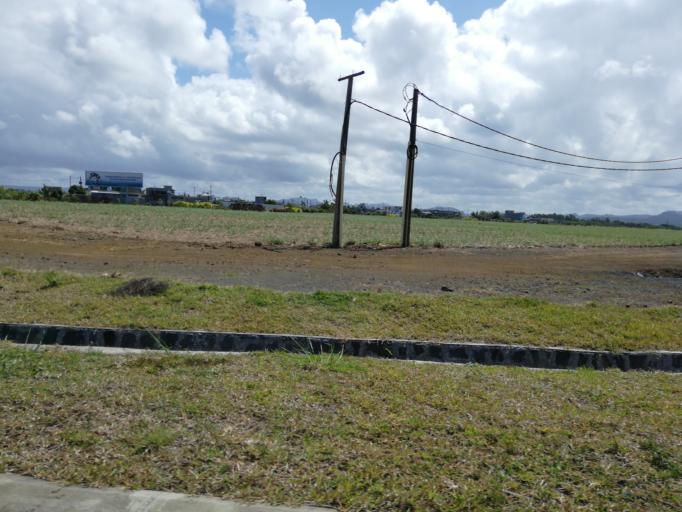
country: MU
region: Grand Port
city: Plaine Magnien
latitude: -20.4416
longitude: 57.6684
